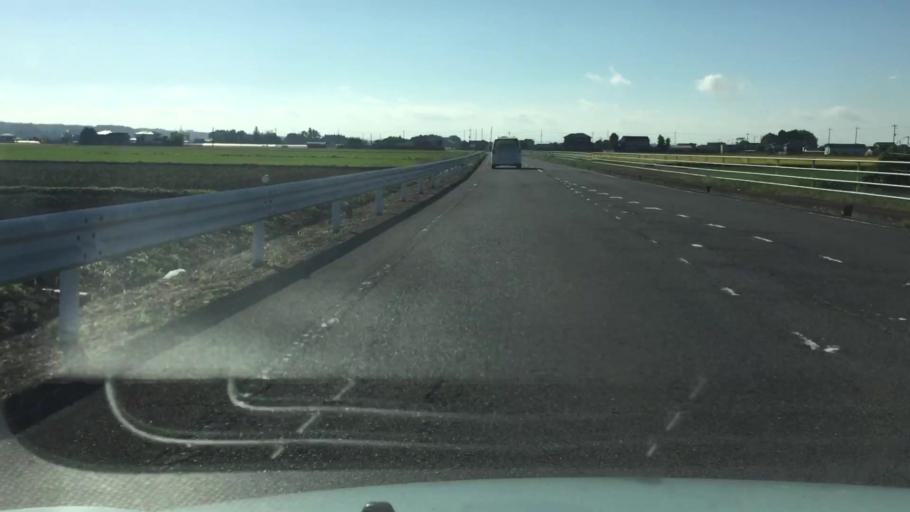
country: JP
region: Tochigi
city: Ujiie
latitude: 36.6753
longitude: 140.0138
